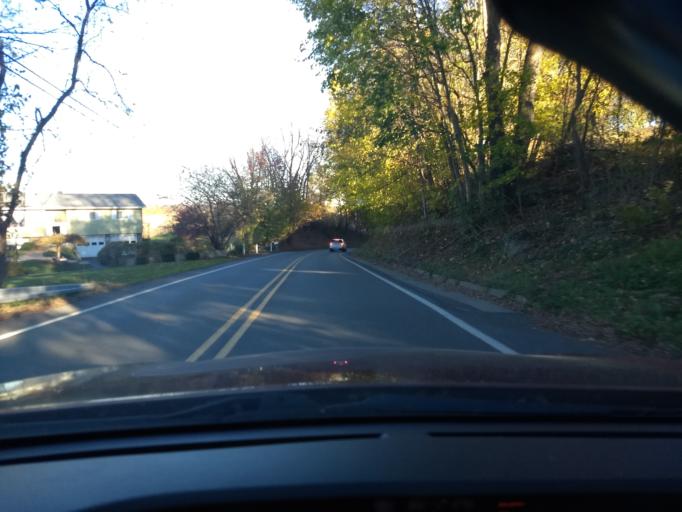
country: US
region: Pennsylvania
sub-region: Allegheny County
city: Rennerdale
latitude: 40.3782
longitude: -80.1595
